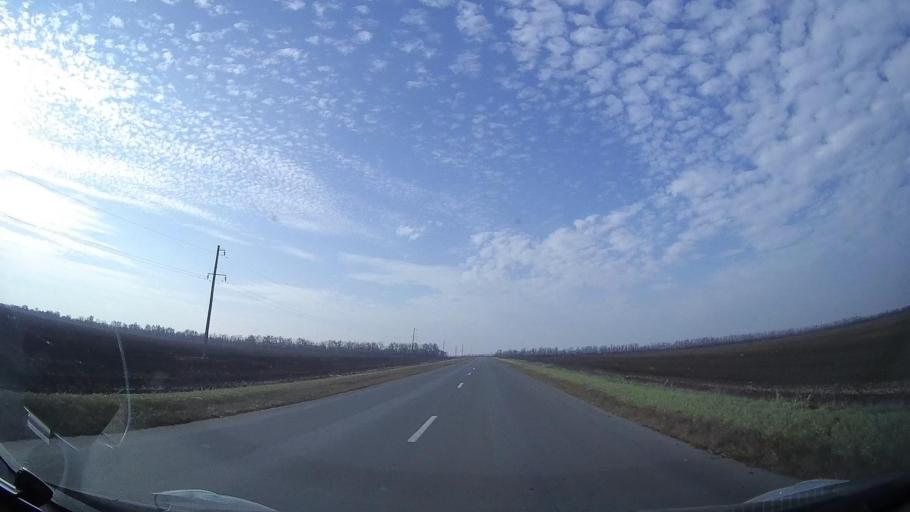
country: RU
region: Rostov
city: Veselyy
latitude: 46.9695
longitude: 40.6619
